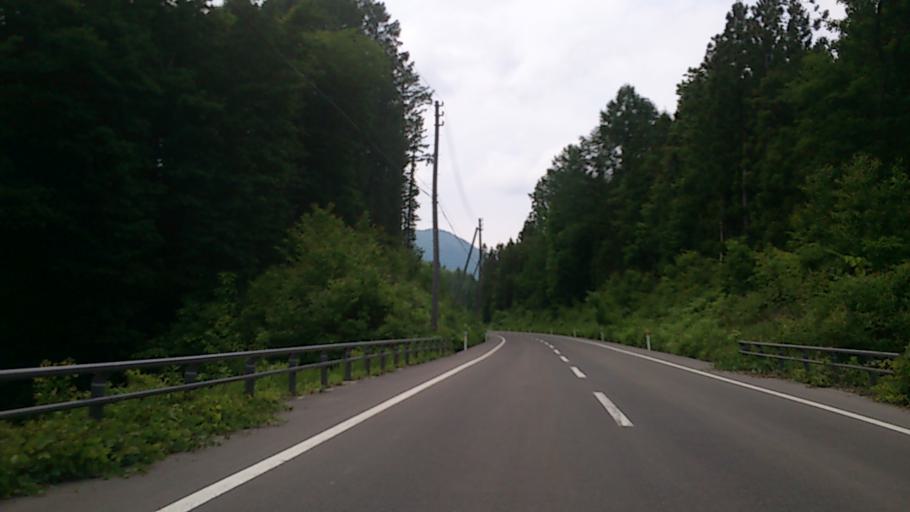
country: JP
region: Aomori
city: Hirosaki
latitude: 40.5200
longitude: 140.2158
